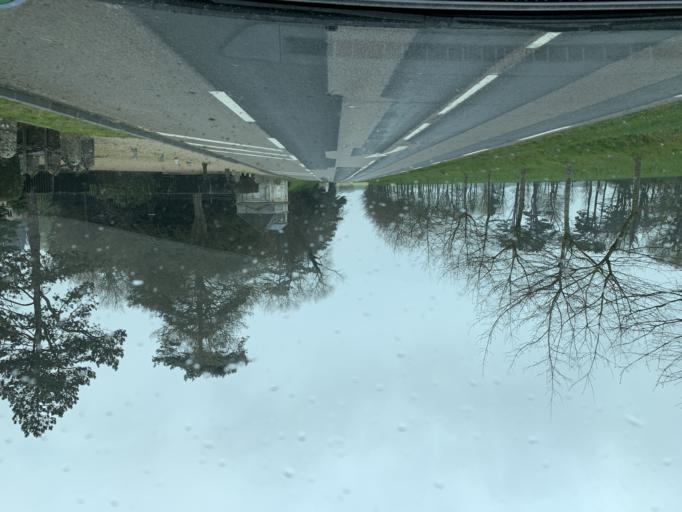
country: FR
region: Haute-Normandie
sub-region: Departement de la Seine-Maritime
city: Etretat
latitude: 49.6920
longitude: 0.2054
